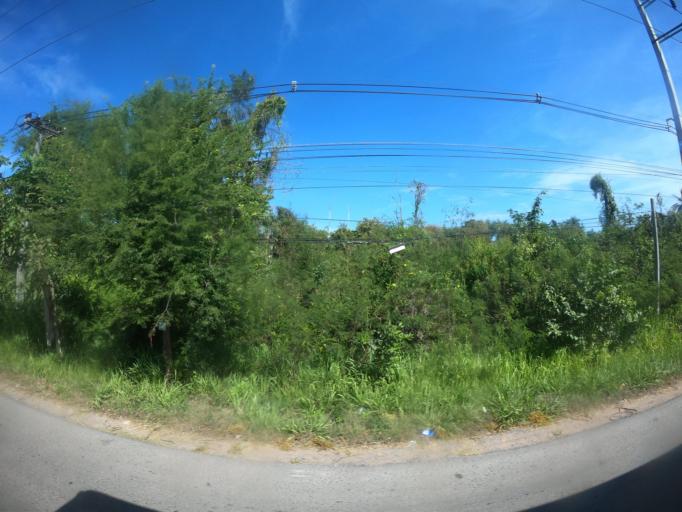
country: TH
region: Khon Kaen
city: Khon Kaen
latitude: 16.4467
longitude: 102.9509
